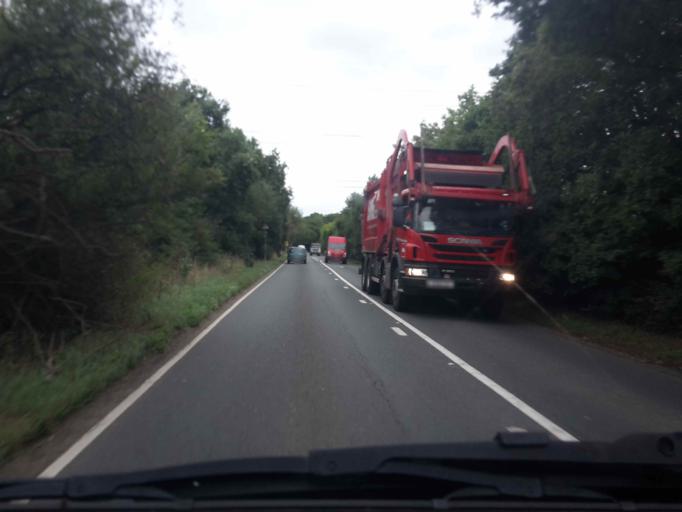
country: GB
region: England
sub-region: Hampshire
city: Eversley
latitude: 51.3449
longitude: -0.8823
